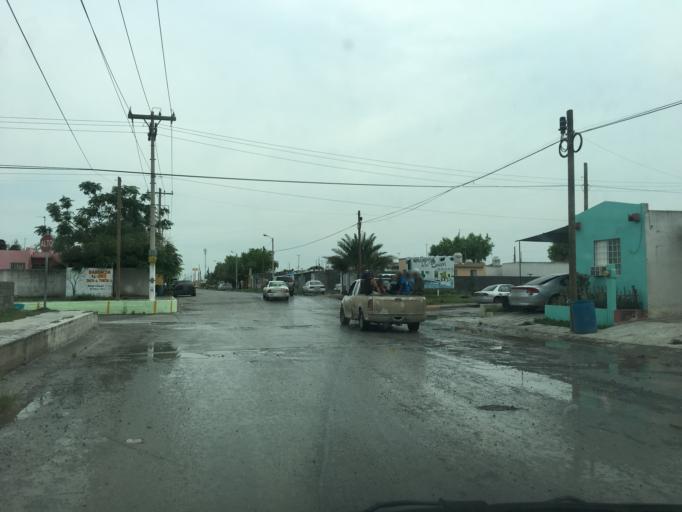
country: MX
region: Tamaulipas
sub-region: Matamoros
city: Heroica Matamoros
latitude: 25.8552
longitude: -97.5620
